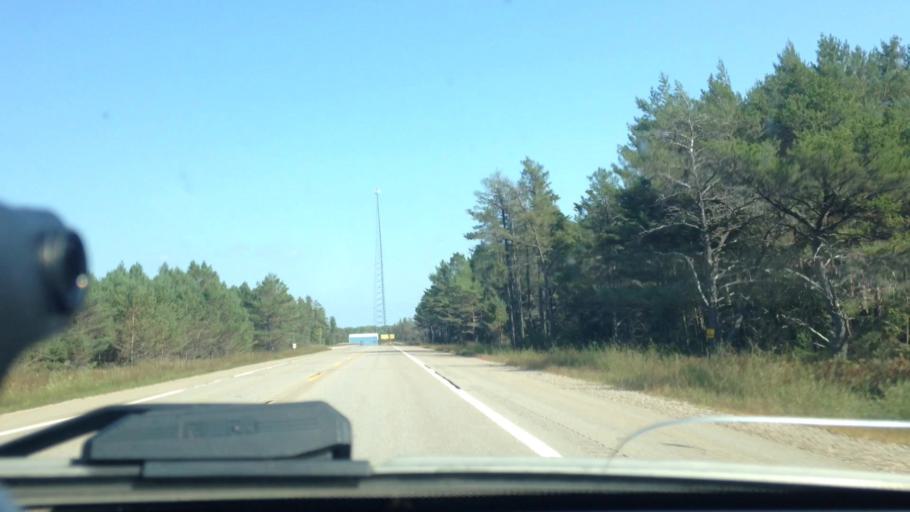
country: US
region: Michigan
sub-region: Chippewa County
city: Sault Ste. Marie
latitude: 46.3589
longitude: -84.8008
